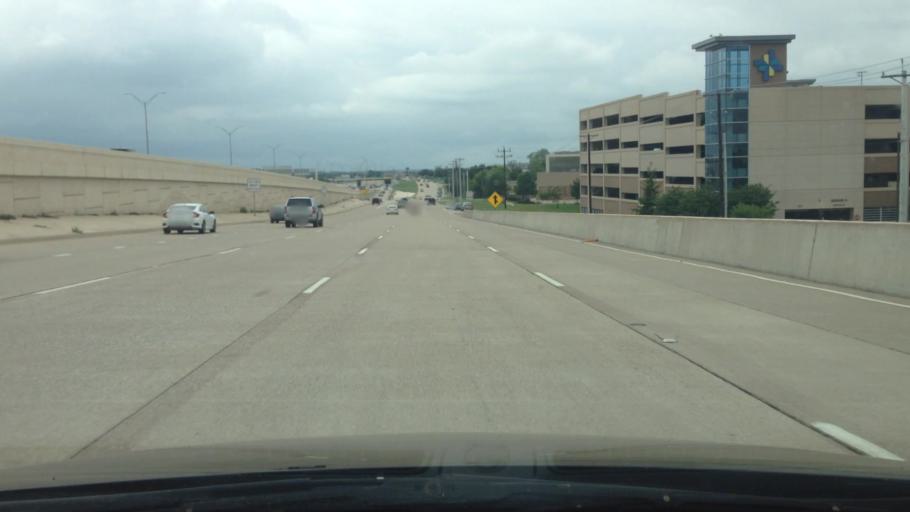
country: US
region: Texas
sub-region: Tarrant County
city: Grapevine
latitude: 32.9322
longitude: -97.0946
